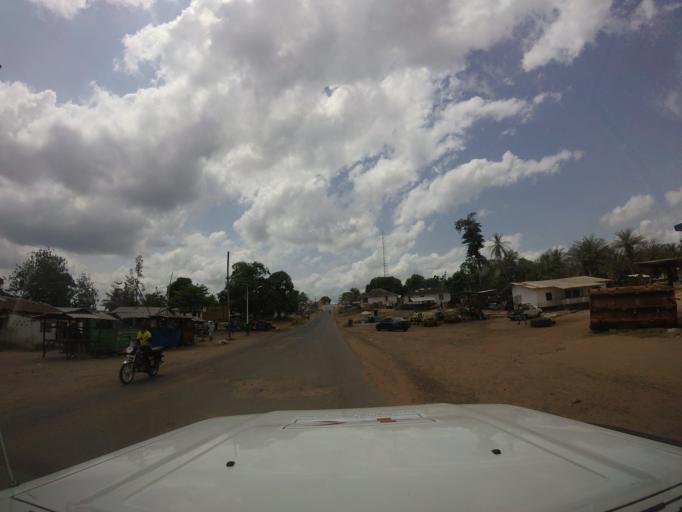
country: LR
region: Bomi
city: Tubmanburg
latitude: 6.8675
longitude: -10.8194
